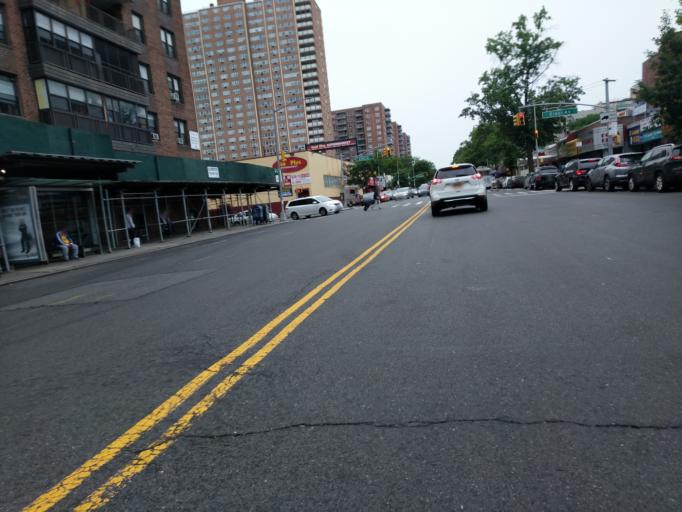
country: US
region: New York
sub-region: Queens County
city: Jamaica
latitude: 40.7529
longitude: -73.8215
